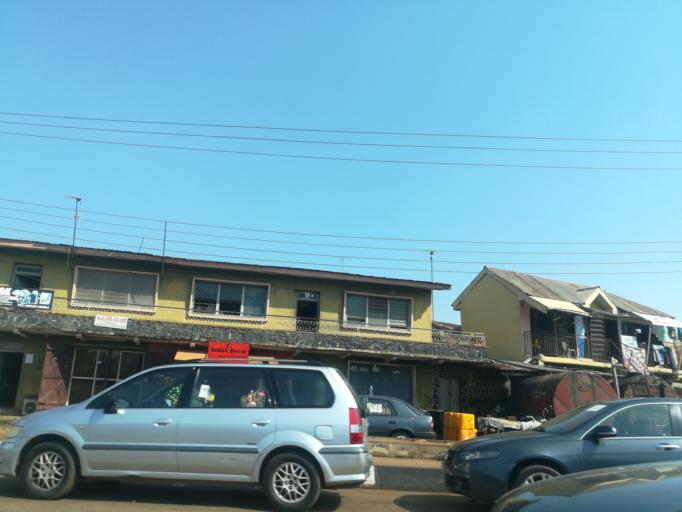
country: NG
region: Ogun
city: Abeokuta
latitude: 7.1478
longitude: 3.3426
